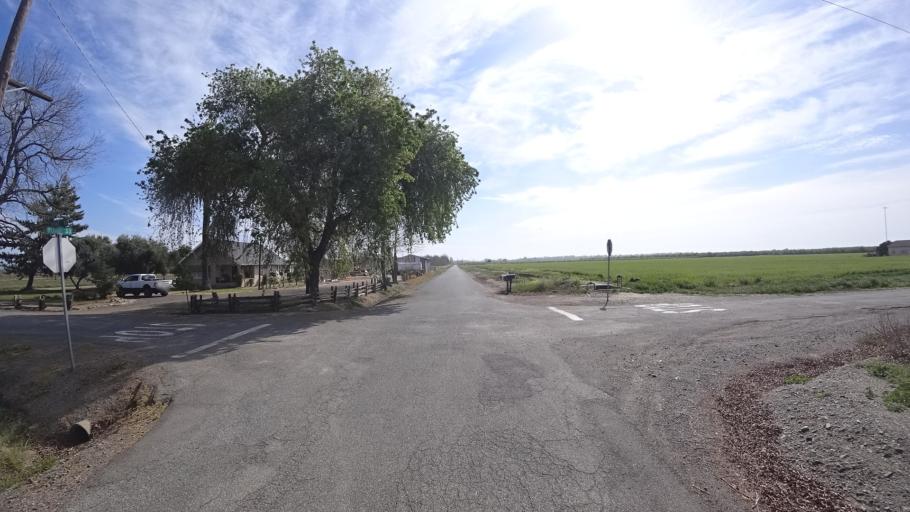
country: US
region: California
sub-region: Glenn County
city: Hamilton City
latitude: 39.6234
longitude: -122.0183
